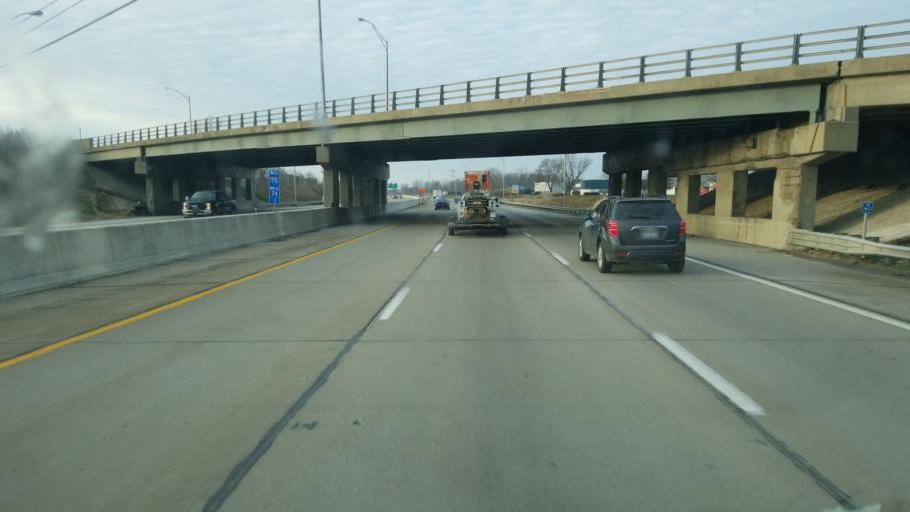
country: US
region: Indiana
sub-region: Marion County
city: Speedway
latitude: 39.7259
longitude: -86.2500
